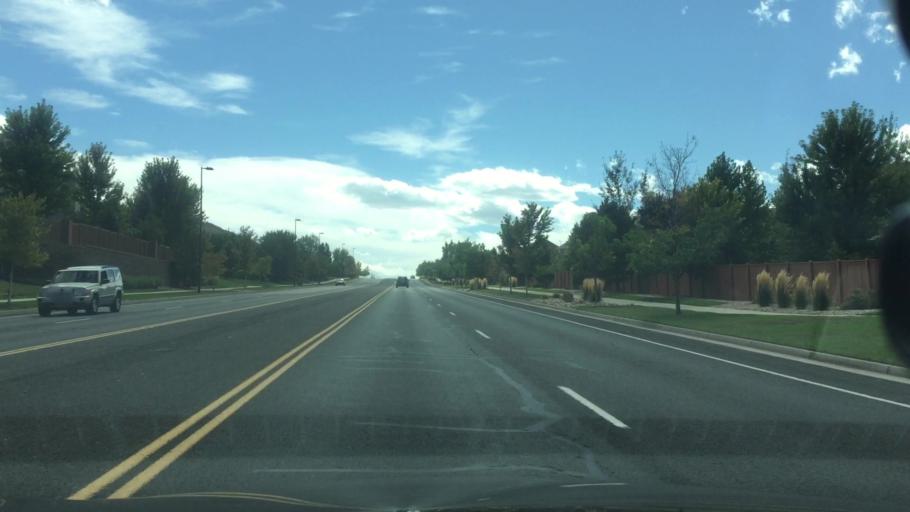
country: US
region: Colorado
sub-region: Arapahoe County
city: Dove Valley
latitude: 39.6452
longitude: -104.7351
